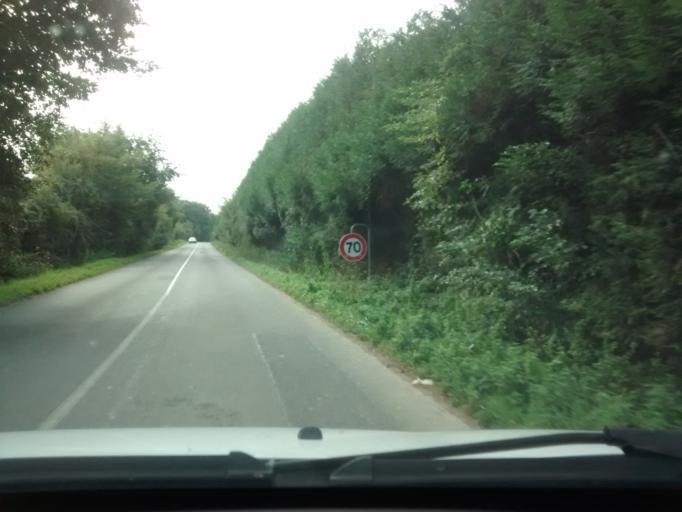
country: FR
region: Brittany
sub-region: Departement d'Ille-et-Vilaine
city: Vezin-le-Coquet
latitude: 48.0846
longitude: -1.7582
